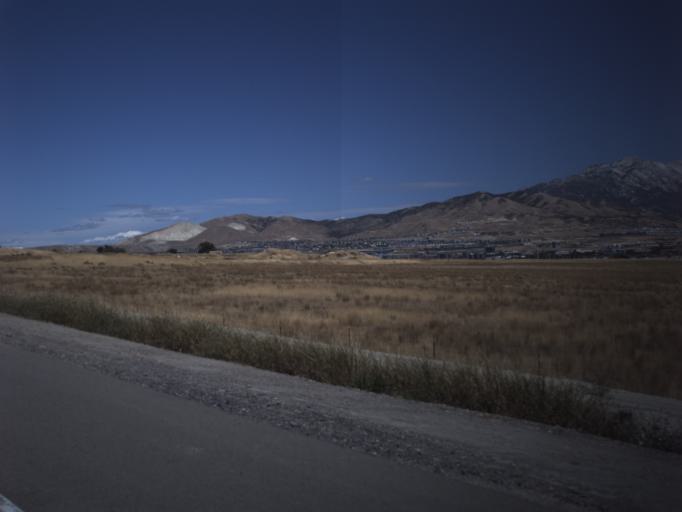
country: US
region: Utah
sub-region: Utah County
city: Saratoga Springs
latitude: 40.3947
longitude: -111.9178
